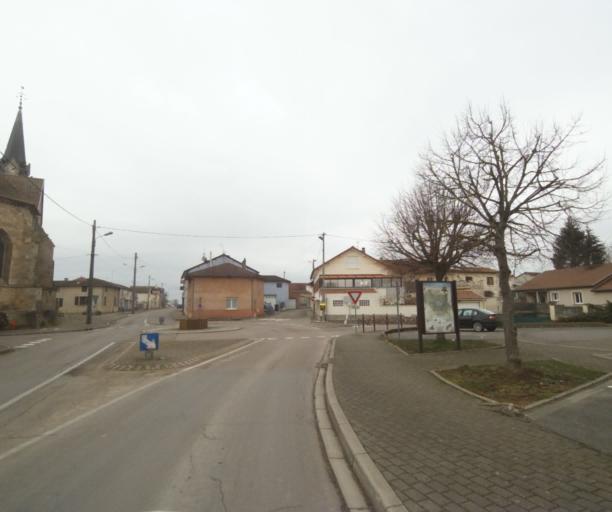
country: FR
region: Champagne-Ardenne
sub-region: Departement de la Haute-Marne
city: Villiers-en-Lieu
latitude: 48.6663
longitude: 4.9012
